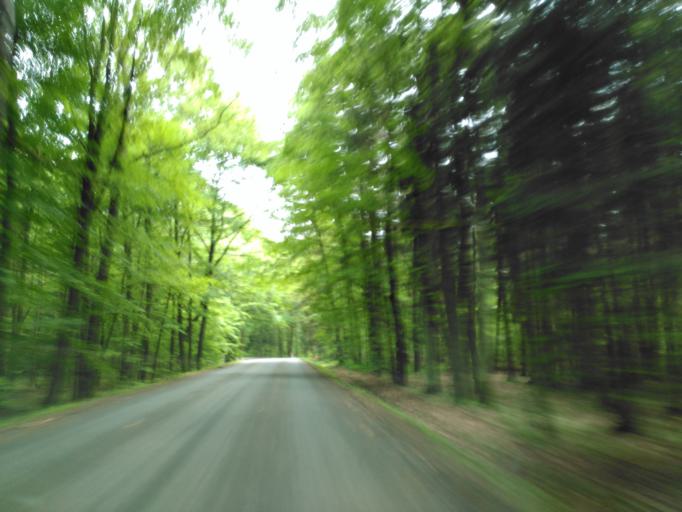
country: CZ
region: Central Bohemia
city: Hudlice
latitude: 49.9500
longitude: 13.9194
